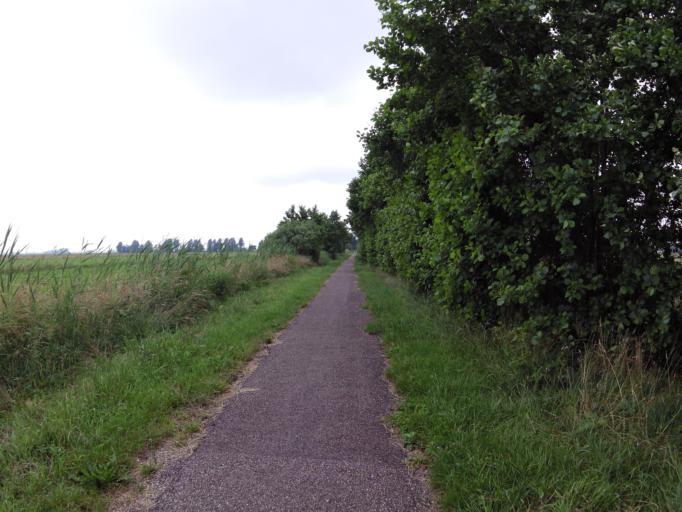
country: NL
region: Utrecht
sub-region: Gemeente Woerden
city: Woerden
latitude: 52.1429
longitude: 4.9290
